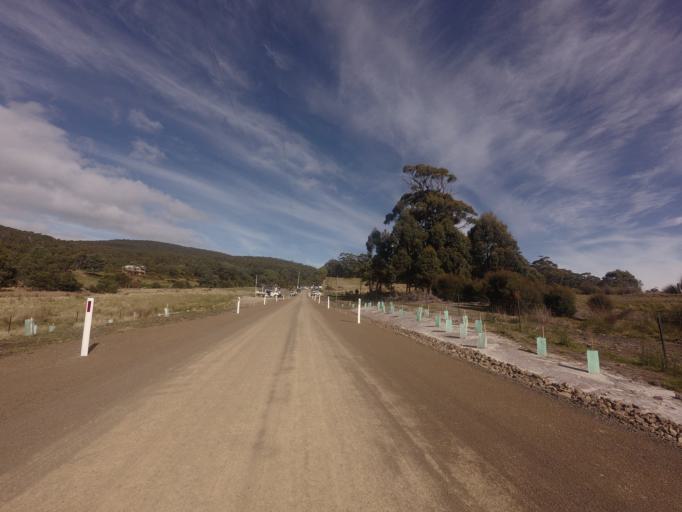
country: AU
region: Tasmania
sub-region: Clarence
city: Sandford
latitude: -43.1931
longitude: 147.7775
